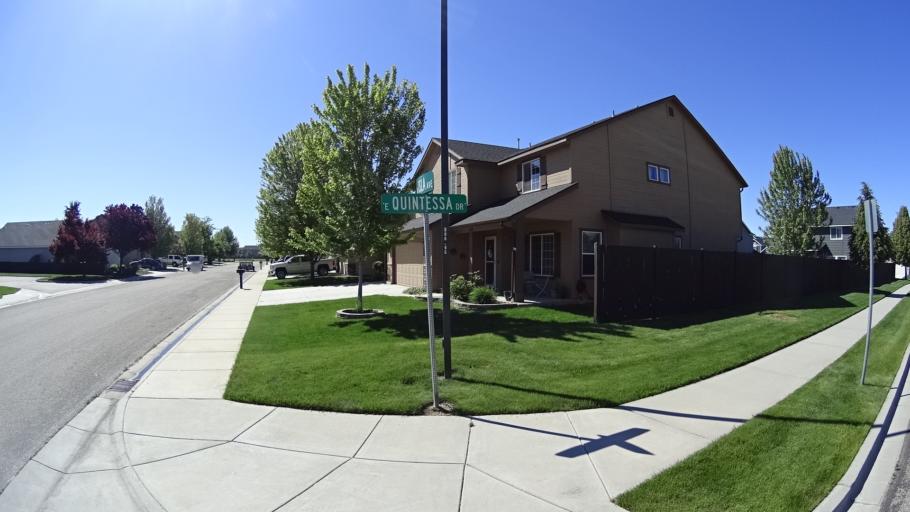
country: US
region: Idaho
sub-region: Ada County
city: Meridian
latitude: 43.6536
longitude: -116.3907
